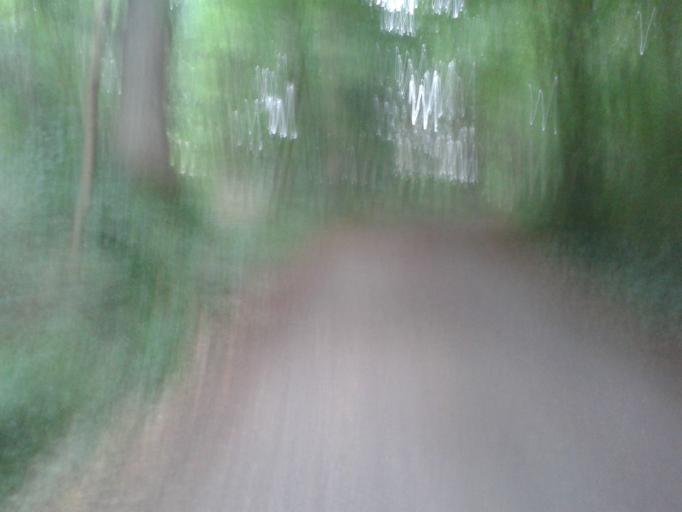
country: GB
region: England
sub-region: Cambridgeshire
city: Sawston
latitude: 52.1583
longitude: 0.1796
